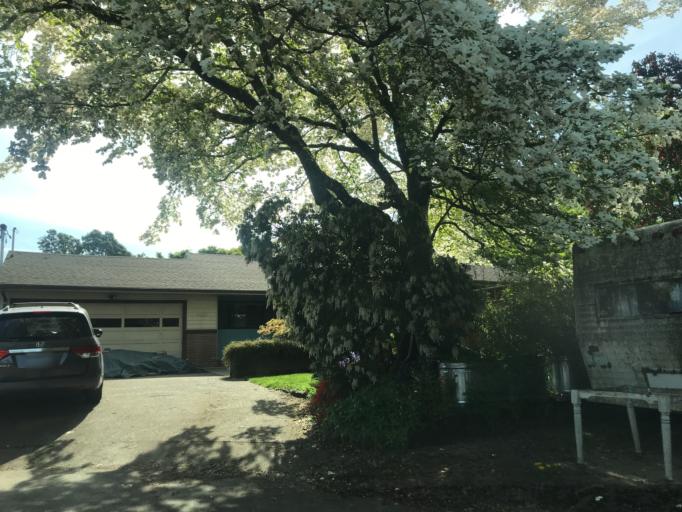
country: US
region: Oregon
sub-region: Multnomah County
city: Lents
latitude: 45.5008
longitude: -122.6005
